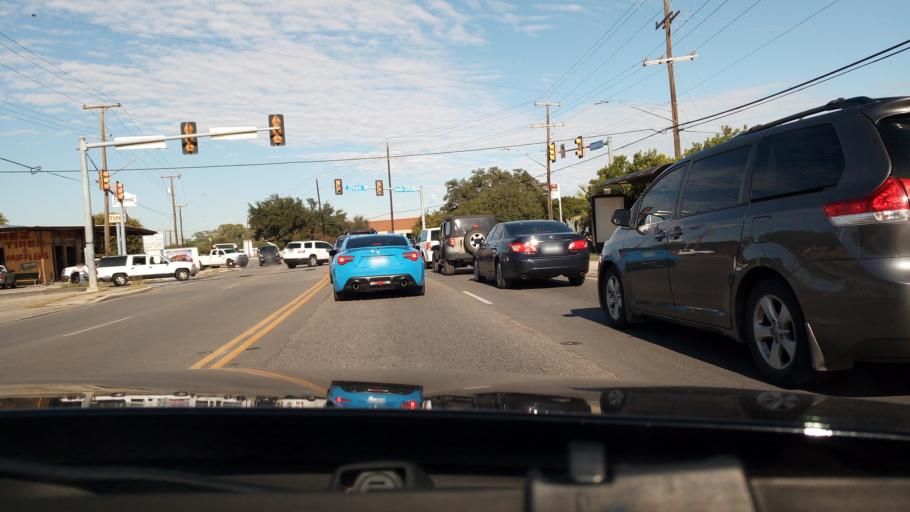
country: US
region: Texas
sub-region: Bexar County
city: Windcrest
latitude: 29.5290
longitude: -98.4325
